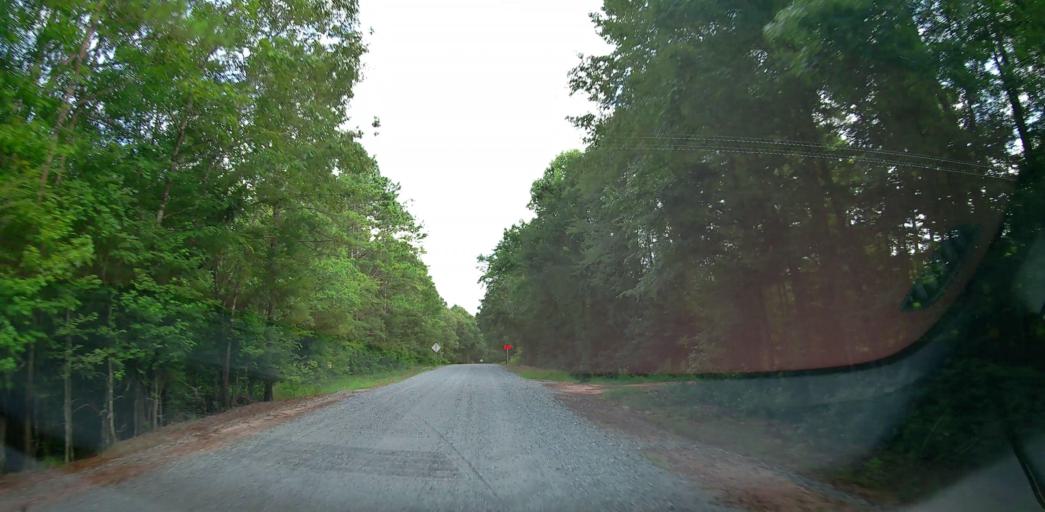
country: US
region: Georgia
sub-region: Bleckley County
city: Cochran
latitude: 32.4217
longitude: -83.4532
